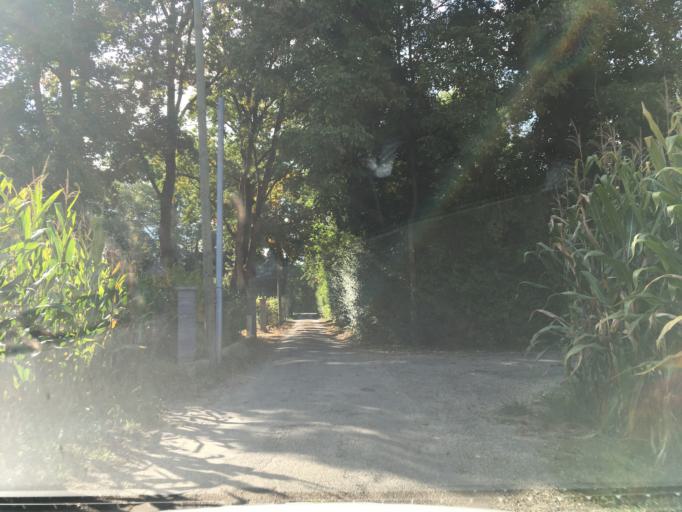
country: FR
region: Alsace
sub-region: Departement du Haut-Rhin
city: Horbourg-Wihr
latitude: 48.0709
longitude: 7.3819
